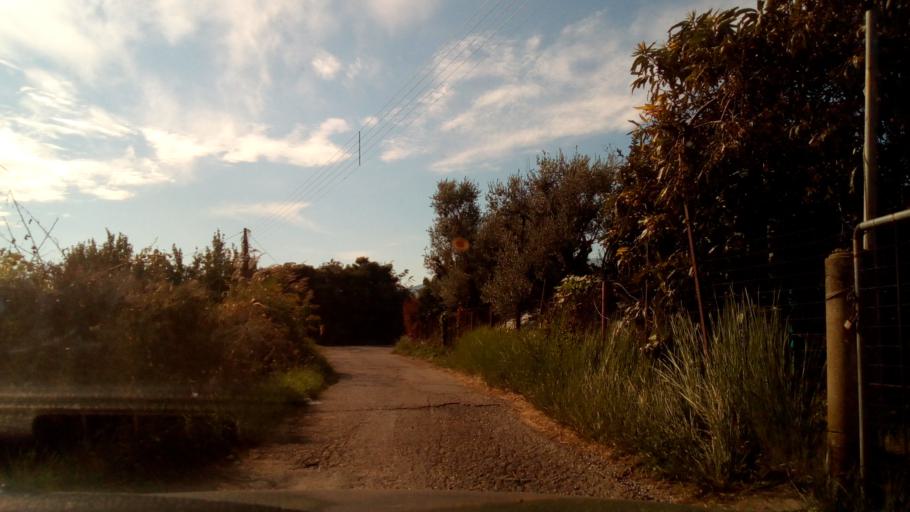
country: GR
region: West Greece
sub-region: Nomos Aitolias kai Akarnanias
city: Nafpaktos
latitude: 38.3977
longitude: 21.9033
